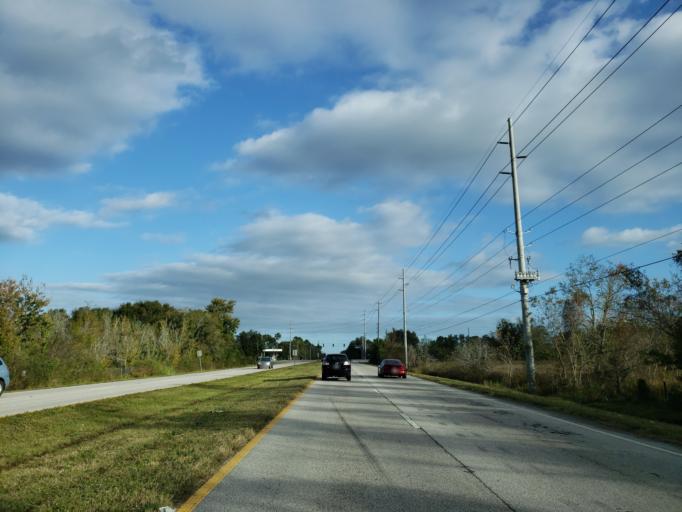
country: US
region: Florida
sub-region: Hillsborough County
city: Plant City
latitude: 28.0051
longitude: -82.1049
